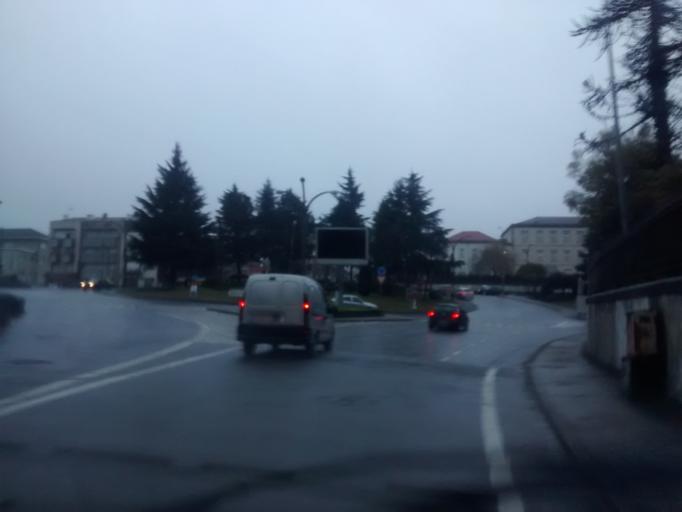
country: PT
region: Braga
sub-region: Braga
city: Braga
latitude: 41.5584
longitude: -8.4181
